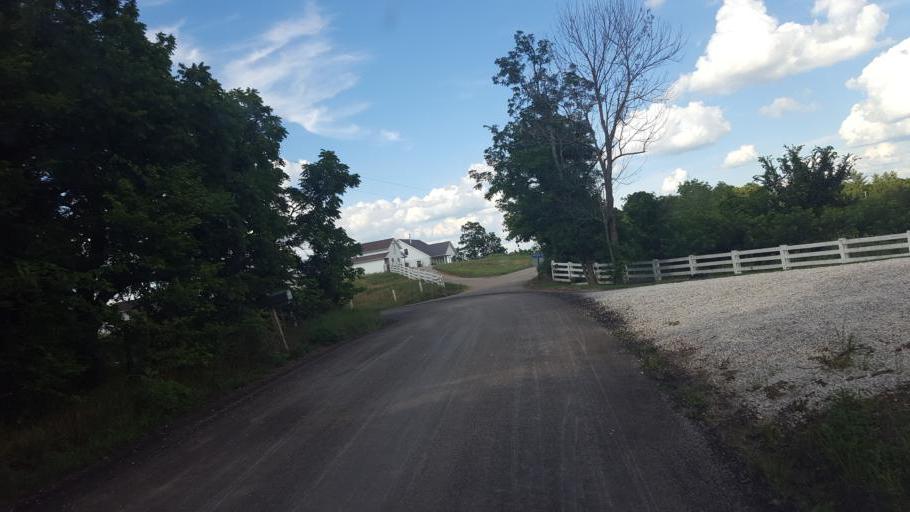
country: US
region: Ohio
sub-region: Gallia County
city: Gallipolis
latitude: 38.7341
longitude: -82.3436
